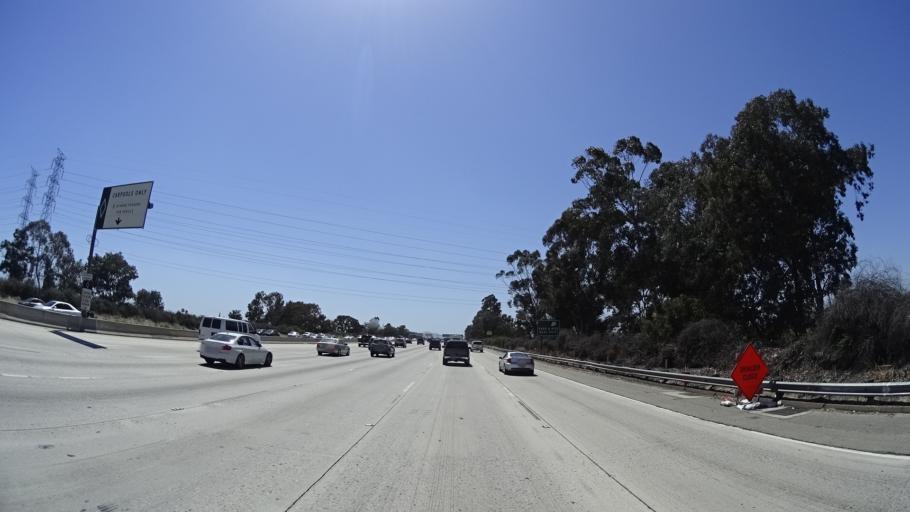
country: US
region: California
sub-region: Los Angeles County
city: San Fernando
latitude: 34.2660
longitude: -118.4549
